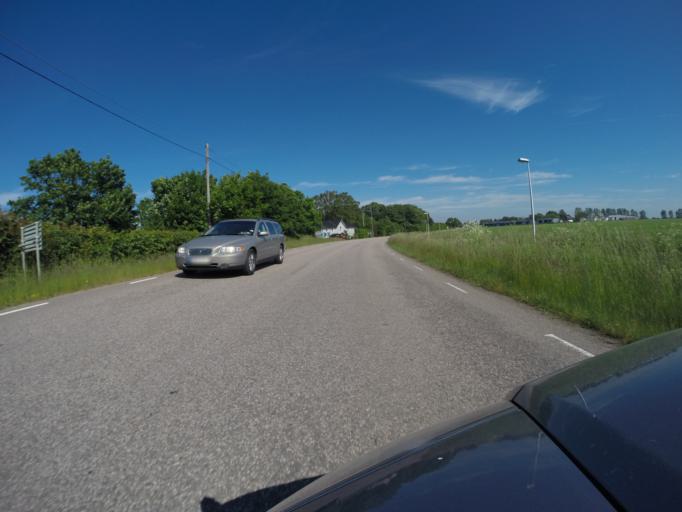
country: SE
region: Skane
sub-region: Helsingborg
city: Odakra
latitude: 56.1109
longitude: 12.7829
